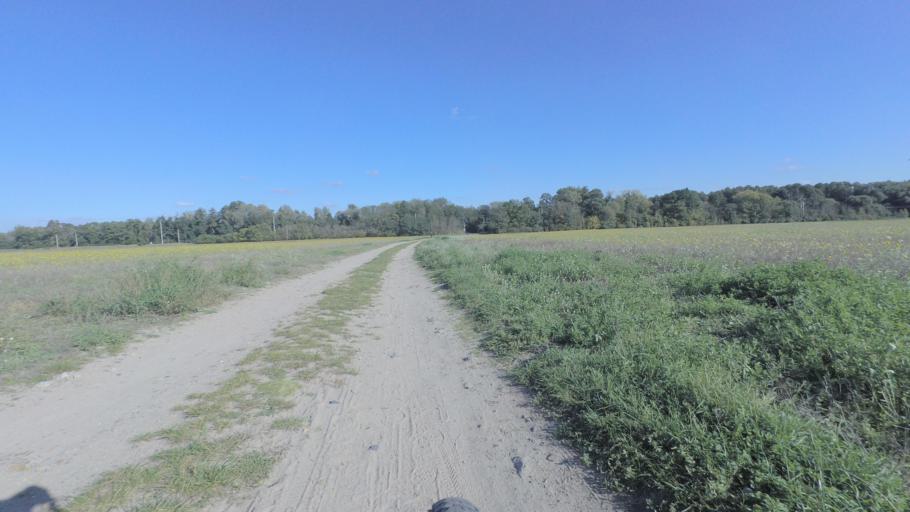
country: DE
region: Brandenburg
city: Rangsdorf
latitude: 52.2733
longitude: 13.4335
